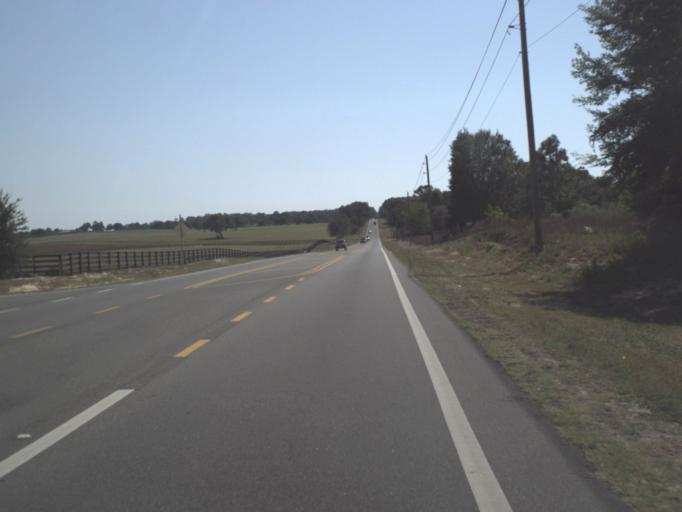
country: US
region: Florida
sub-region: Marion County
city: Dunnellon
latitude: 29.1572
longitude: -82.3538
